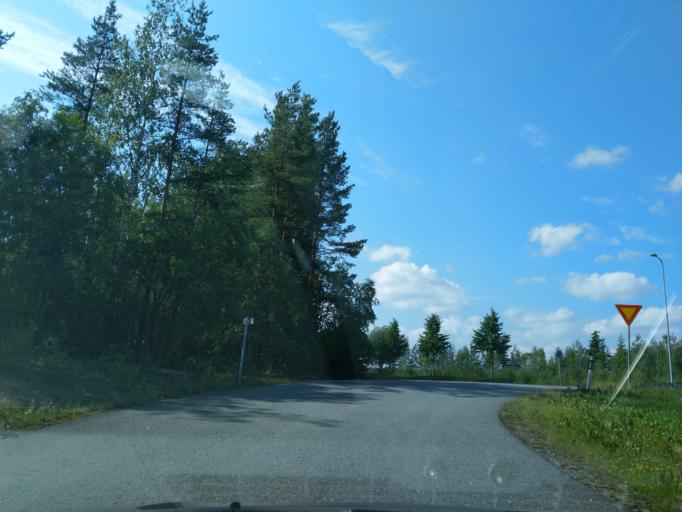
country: FI
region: South Karelia
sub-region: Lappeenranta
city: Lappeenranta
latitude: 61.0371
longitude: 28.1231
